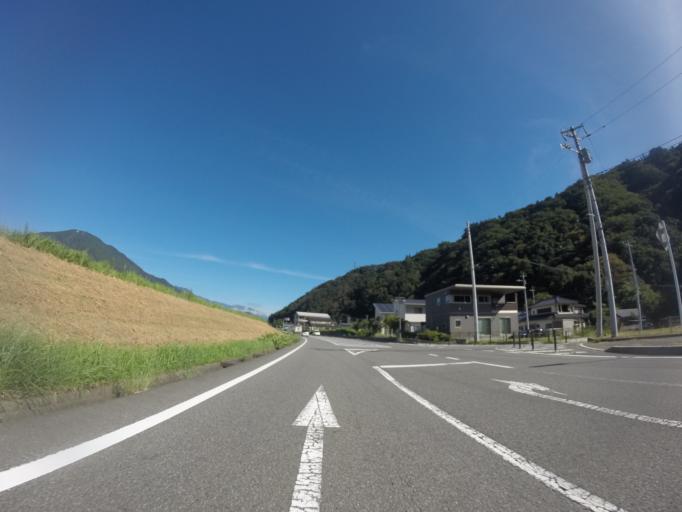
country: JP
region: Shizuoka
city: Fujinomiya
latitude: 35.3687
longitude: 138.4540
